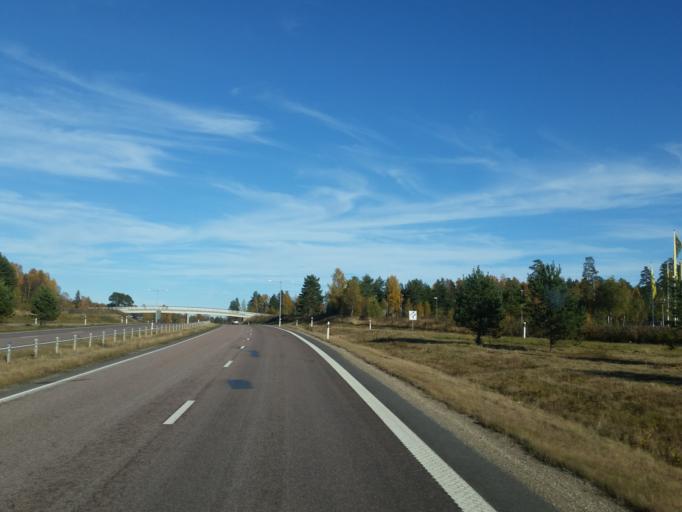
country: SE
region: Dalarna
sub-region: Faluns Kommun
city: Falun
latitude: 60.5764
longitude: 15.6044
